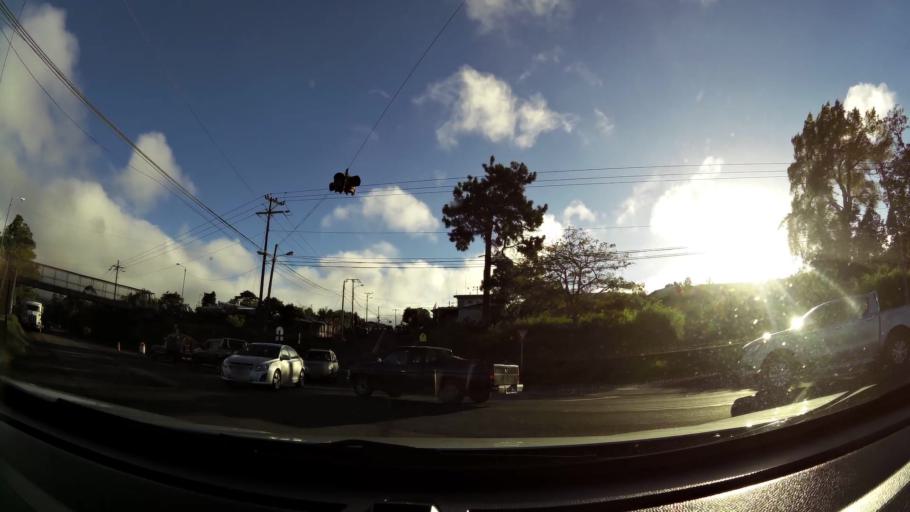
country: CR
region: Heredia
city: Angeles
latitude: 10.0080
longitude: -84.0317
